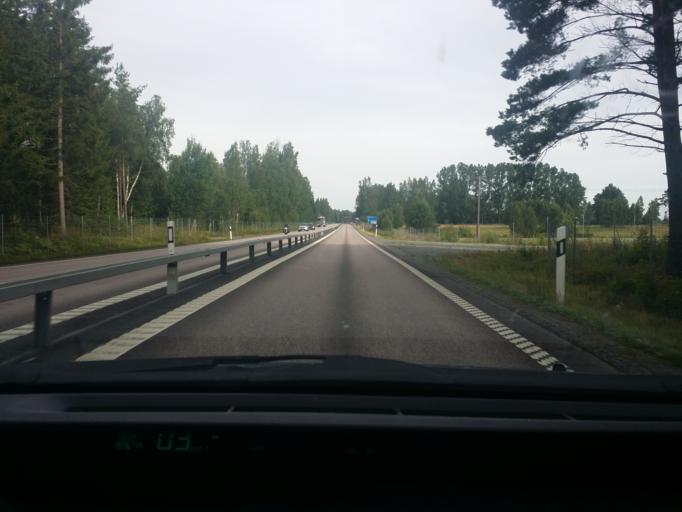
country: SE
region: Vaestmanland
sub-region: Sala Kommun
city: Sala
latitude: 59.8232
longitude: 16.5367
